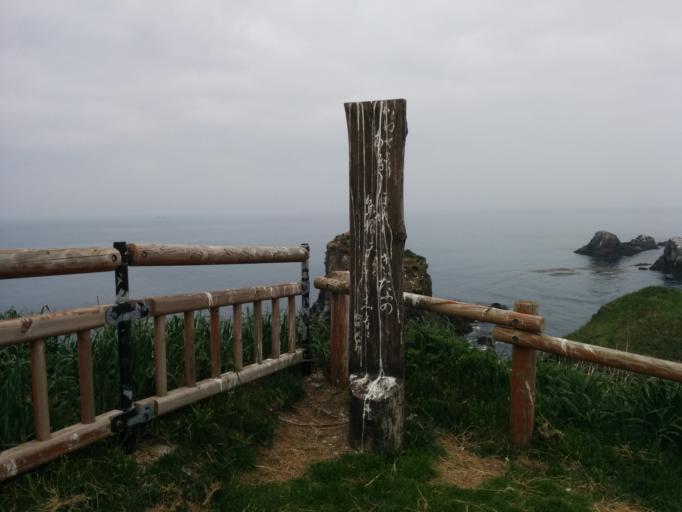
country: JP
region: Hokkaido
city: Nemuro
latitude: 43.0785
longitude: 145.1641
